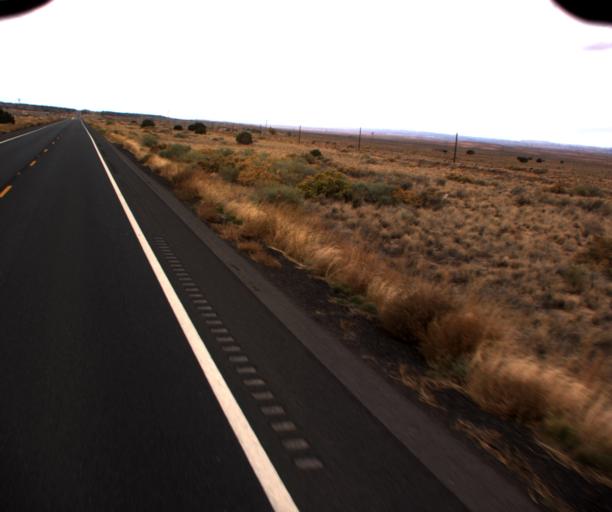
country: US
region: Arizona
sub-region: Coconino County
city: Kaibito
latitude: 36.4667
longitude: -110.6791
